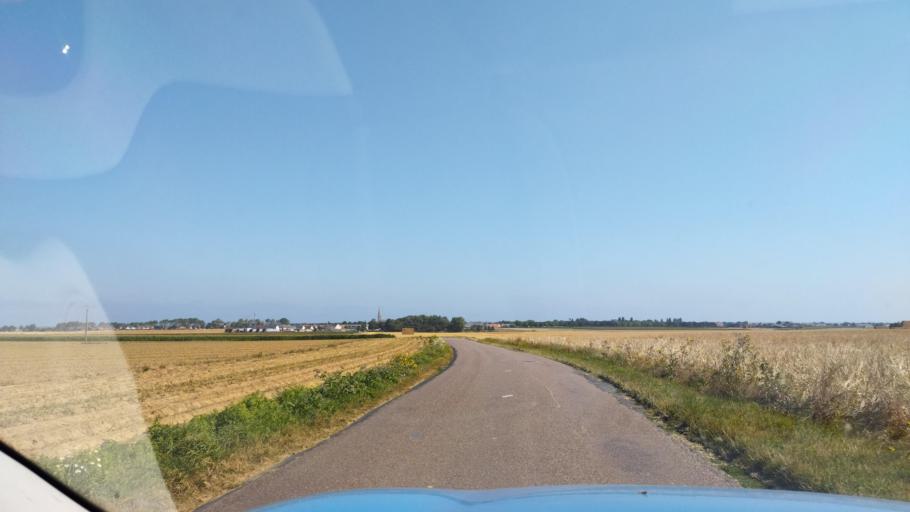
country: FR
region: Lower Normandy
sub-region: Departement du Calvados
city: Saint-Aubin-sur-Mer
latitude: 49.3144
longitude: -0.4036
